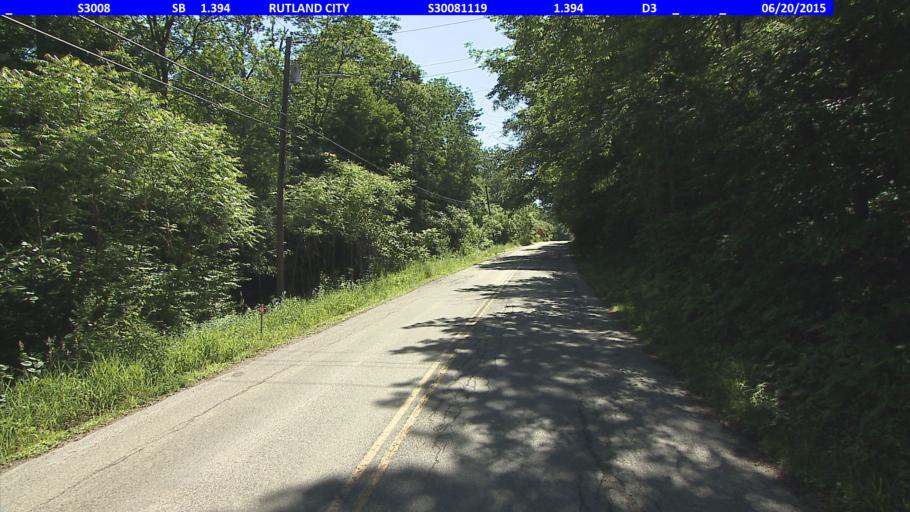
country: US
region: Vermont
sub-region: Rutland County
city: Rutland
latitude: 43.6025
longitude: -72.9974
